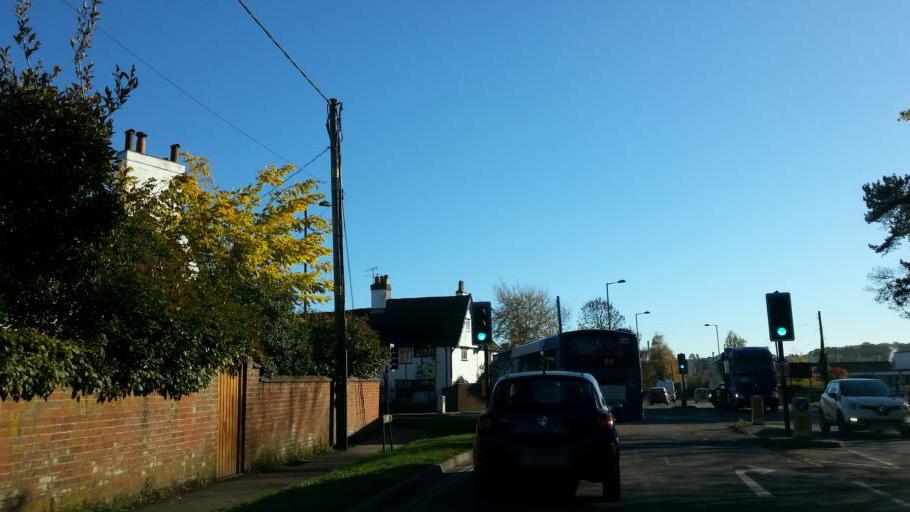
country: GB
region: England
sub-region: Suffolk
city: Woodbridge
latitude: 52.1052
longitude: 1.3293
